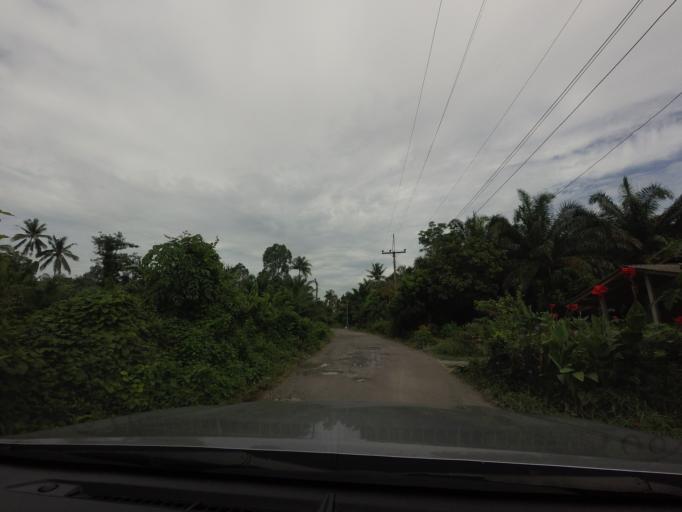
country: TH
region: Nakhon Si Thammarat
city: Phra Phrom
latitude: 8.2831
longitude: 99.9252
